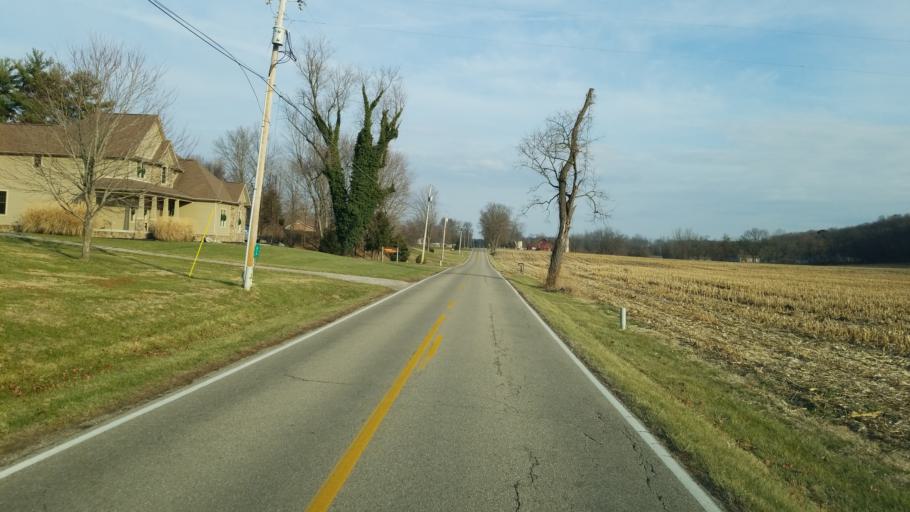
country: US
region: Ohio
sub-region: Ross County
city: Kingston
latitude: 39.4154
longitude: -82.9405
